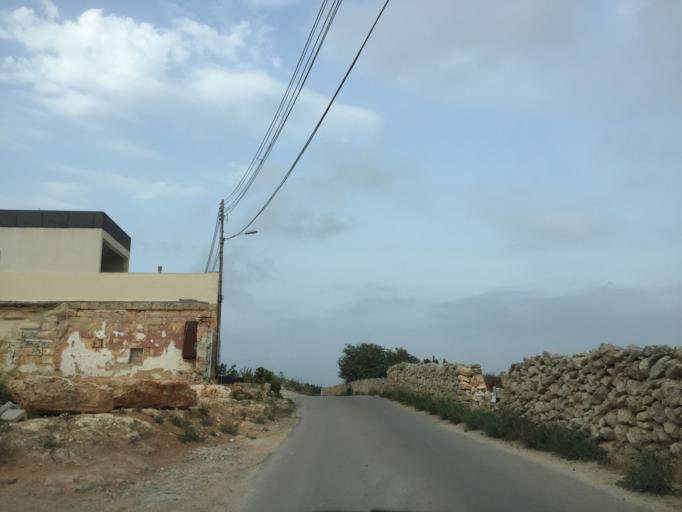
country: MT
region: L-Imgarr
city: Imgarr
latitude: 35.9300
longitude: 14.3846
